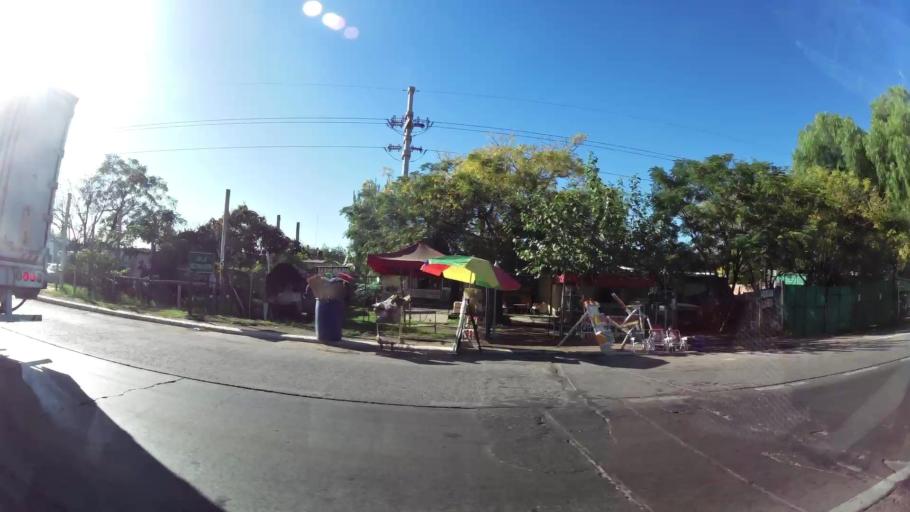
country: AR
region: Mendoza
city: Las Heras
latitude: -32.8705
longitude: -68.8152
